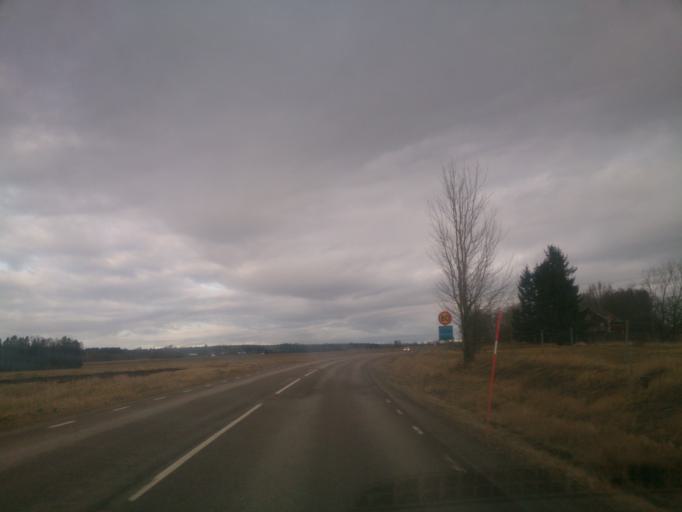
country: SE
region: OEstergoetland
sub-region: Motala Kommun
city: Borensberg
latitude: 58.4805
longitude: 15.2177
